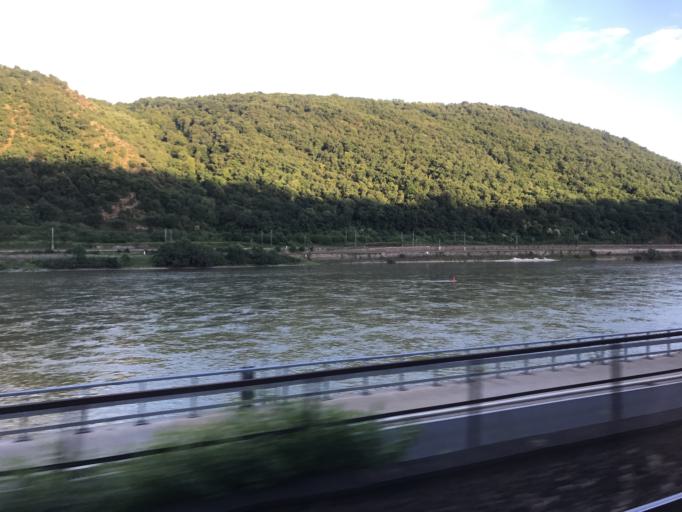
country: DE
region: Rheinland-Pfalz
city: Oberwesel
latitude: 50.1227
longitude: 7.7285
